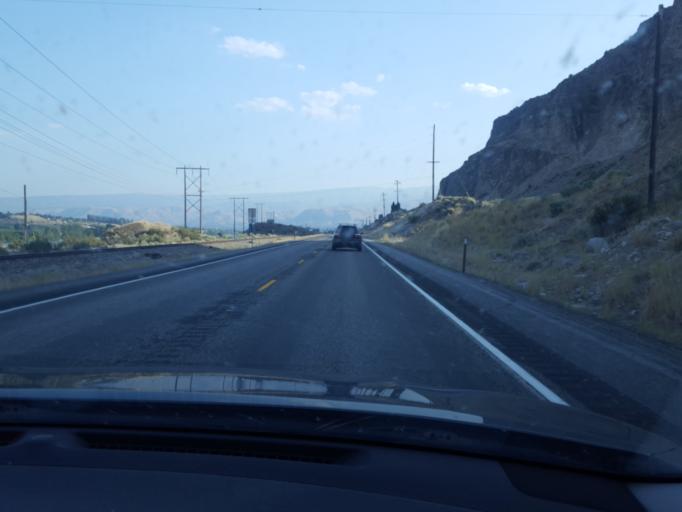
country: US
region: Washington
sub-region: Chelan County
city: Sunnyslope
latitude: 47.5027
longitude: -120.3111
